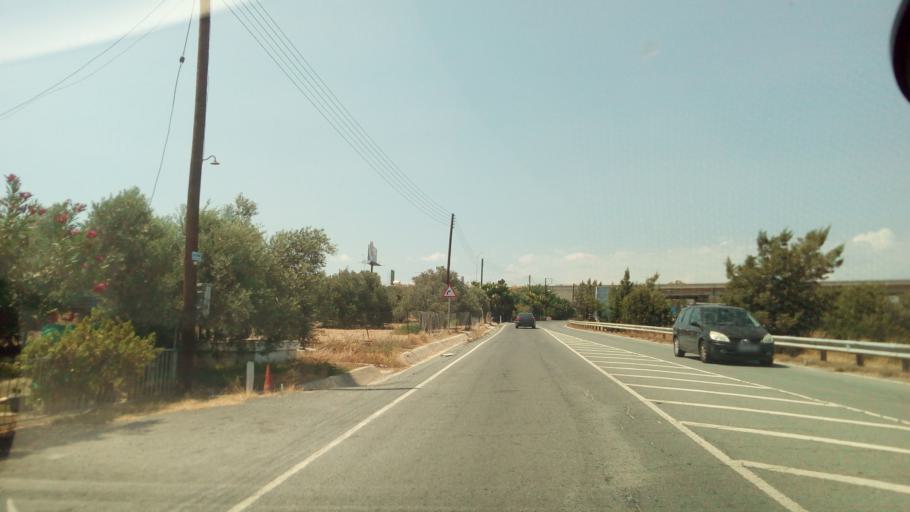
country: CY
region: Limassol
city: Erimi
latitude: 34.6833
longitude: 32.9102
